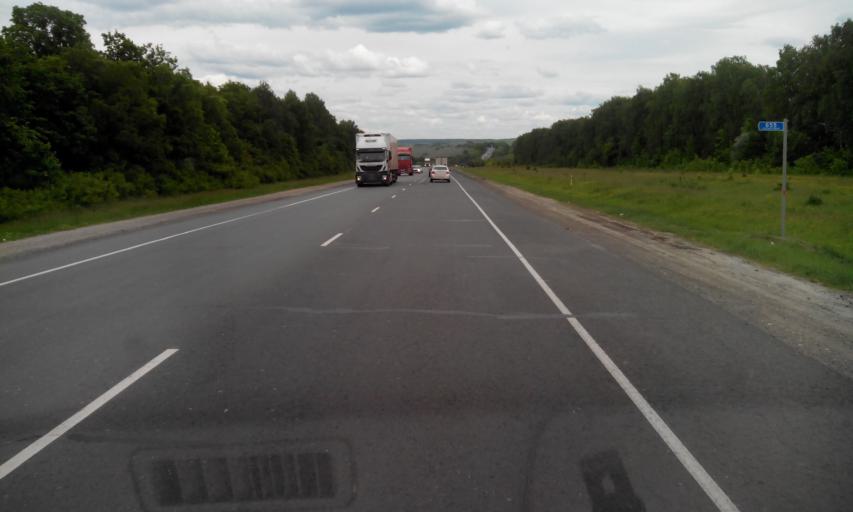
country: RU
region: Penza
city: Chemodanovka
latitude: 53.2219
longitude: 45.3206
